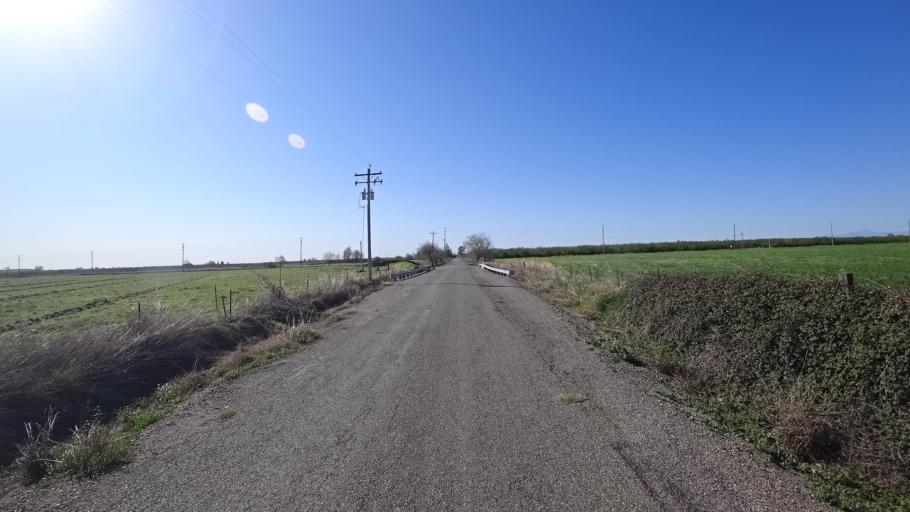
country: US
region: California
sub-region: Glenn County
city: Hamilton City
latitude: 39.7774
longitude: -122.0477
